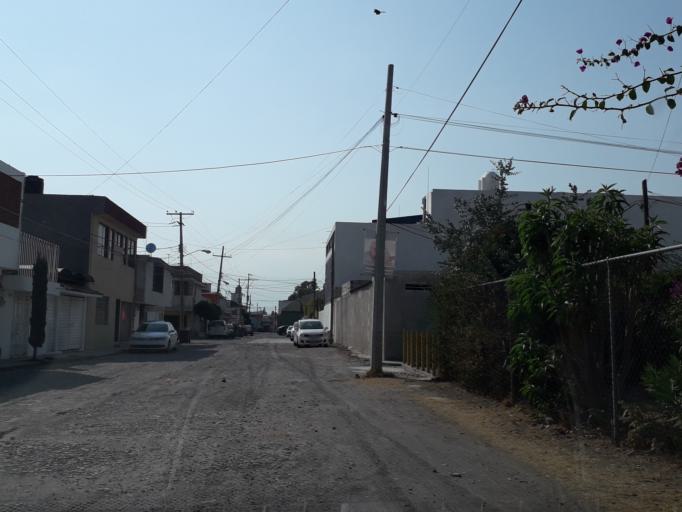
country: MX
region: Puebla
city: Puebla
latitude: 19.0146
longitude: -98.2109
